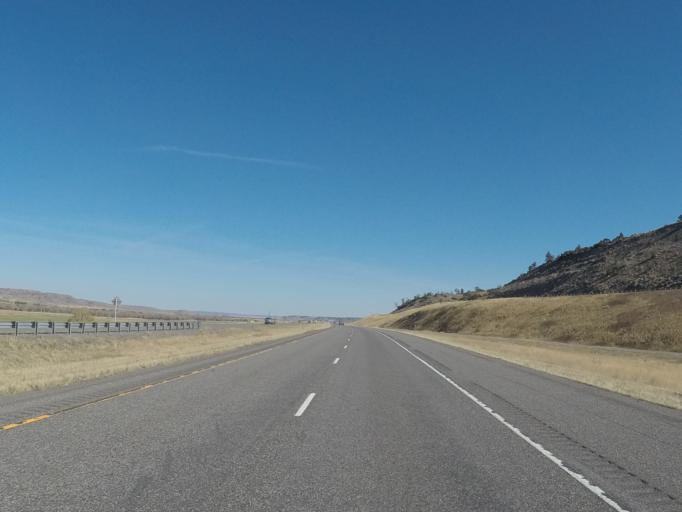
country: US
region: Montana
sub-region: Sweet Grass County
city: Big Timber
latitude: 45.7371
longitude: -110.2140
